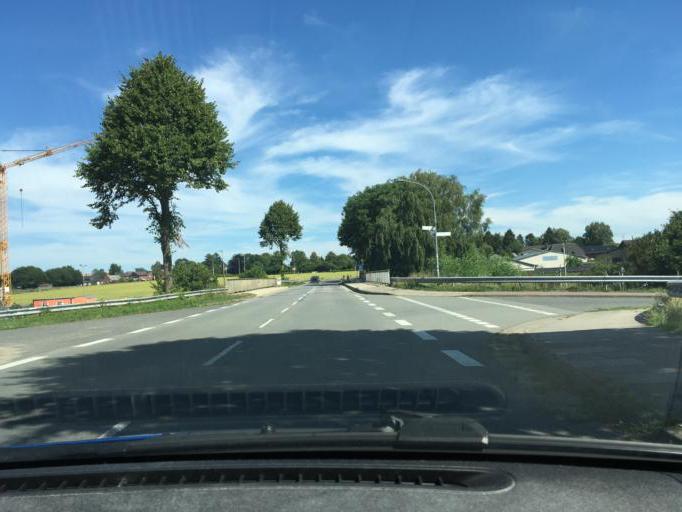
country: DE
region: Lower Saxony
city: Bendestorf
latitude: 53.3673
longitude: 9.9284
